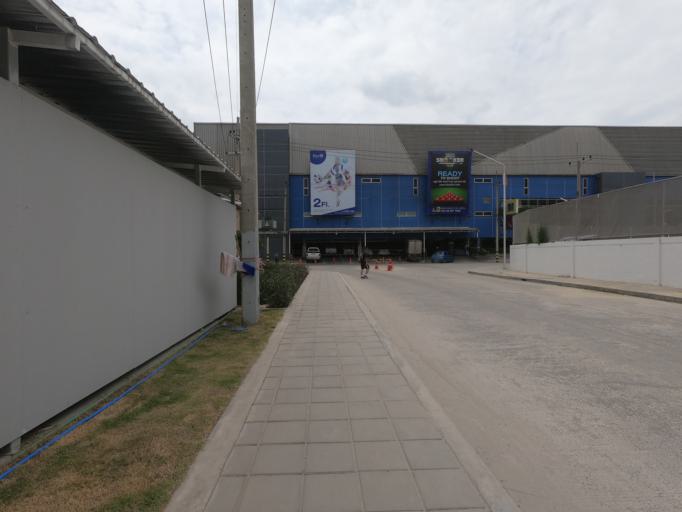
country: TH
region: Bangkok
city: Sai Mai
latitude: 13.9414
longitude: 100.6517
